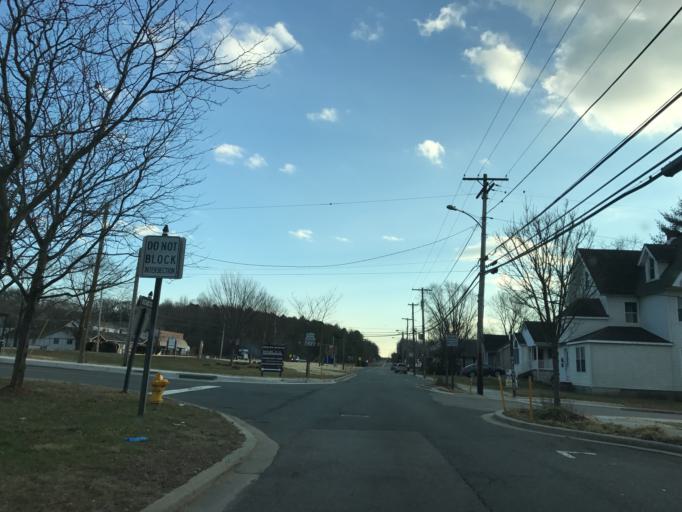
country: US
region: Maryland
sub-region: Cecil County
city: North East
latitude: 39.5939
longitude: -75.9414
